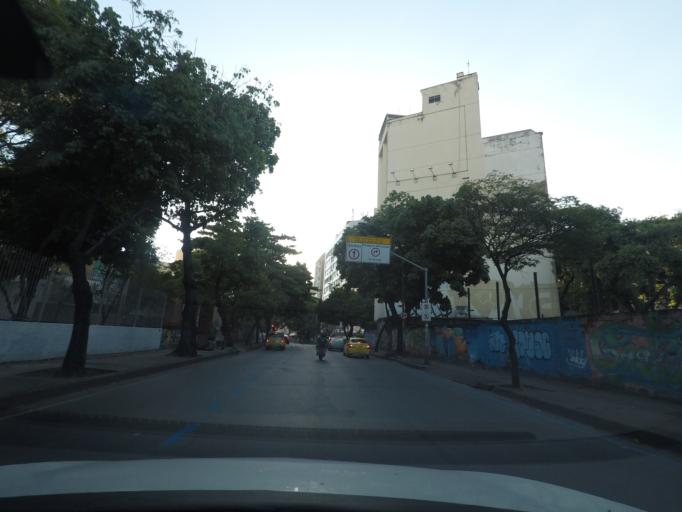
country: BR
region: Rio de Janeiro
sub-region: Rio De Janeiro
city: Rio de Janeiro
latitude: -22.9221
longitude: -43.2295
